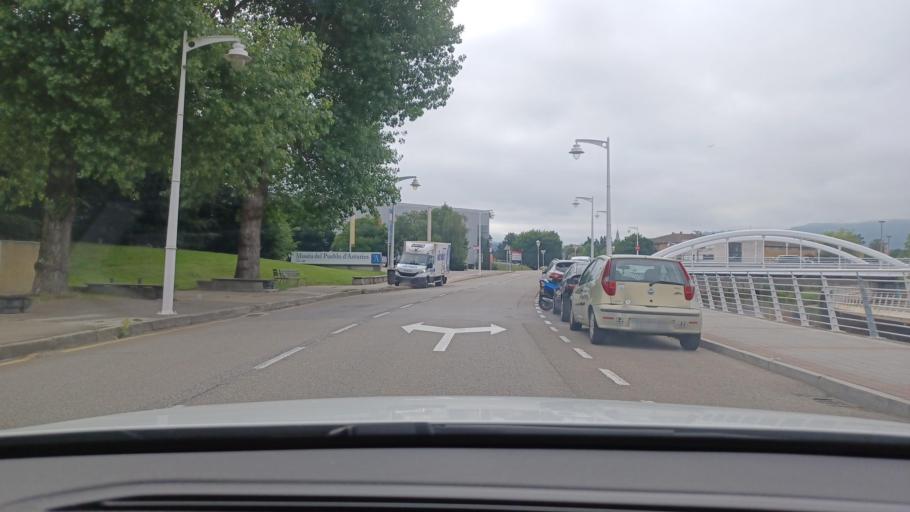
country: ES
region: Asturias
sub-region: Province of Asturias
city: Gijon
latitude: 43.5369
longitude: -5.6357
